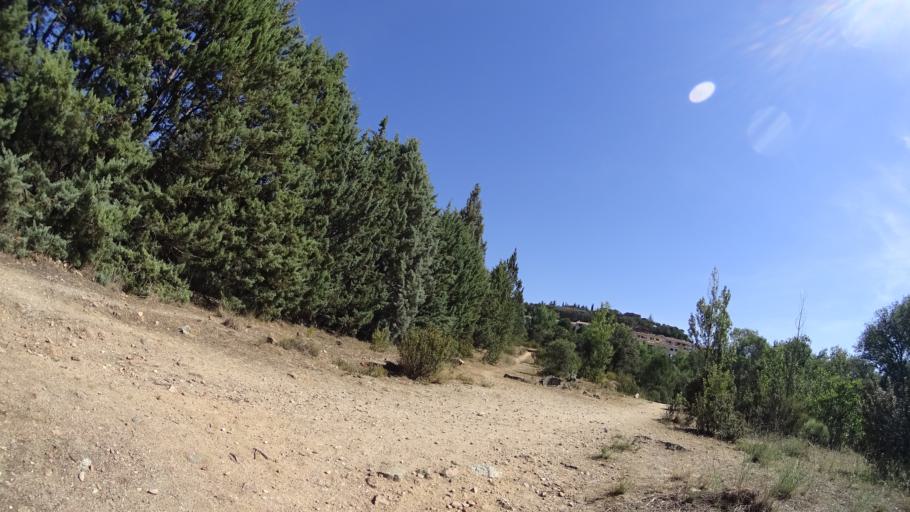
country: ES
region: Madrid
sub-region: Provincia de Madrid
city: Galapagar
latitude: 40.5891
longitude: -3.9657
